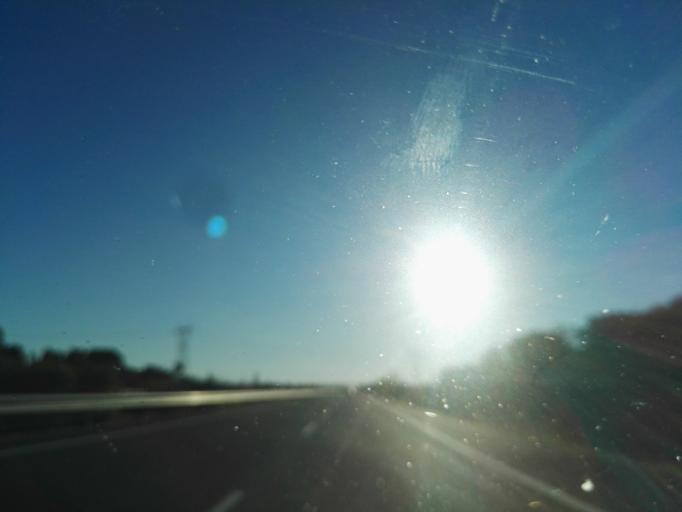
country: PT
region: Evora
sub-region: Evora
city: Evora
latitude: 38.7207
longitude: -7.7804
